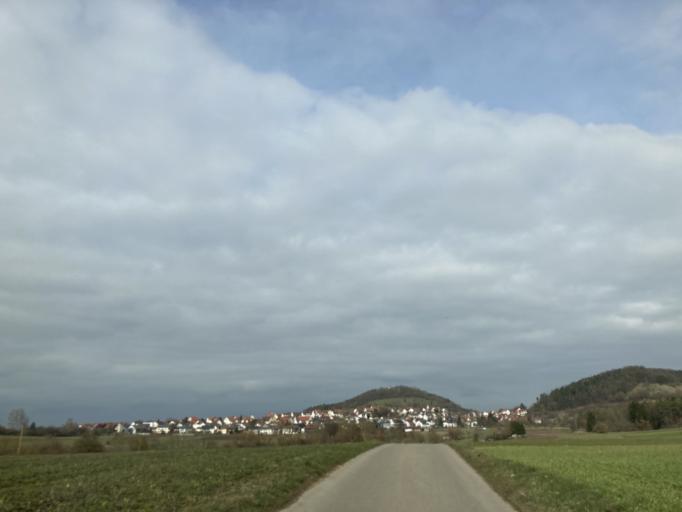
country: DE
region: Baden-Wuerttemberg
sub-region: Tuebingen Region
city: Hirrlingen
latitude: 48.4417
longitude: 8.9133
